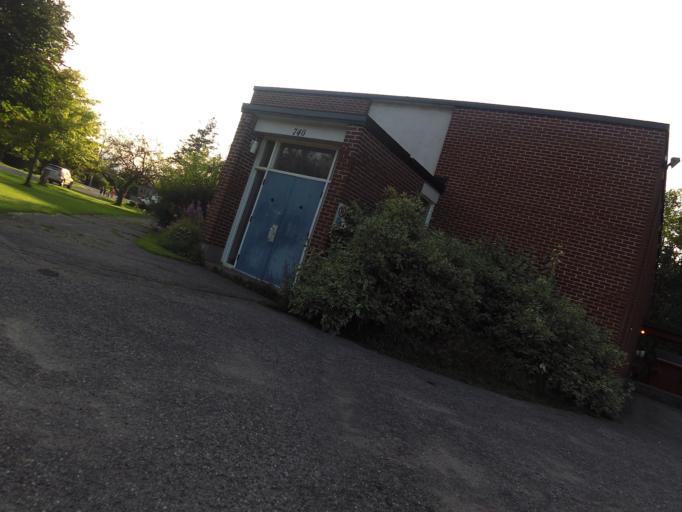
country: CA
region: Ontario
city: Ottawa
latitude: 45.3660
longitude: -75.6994
